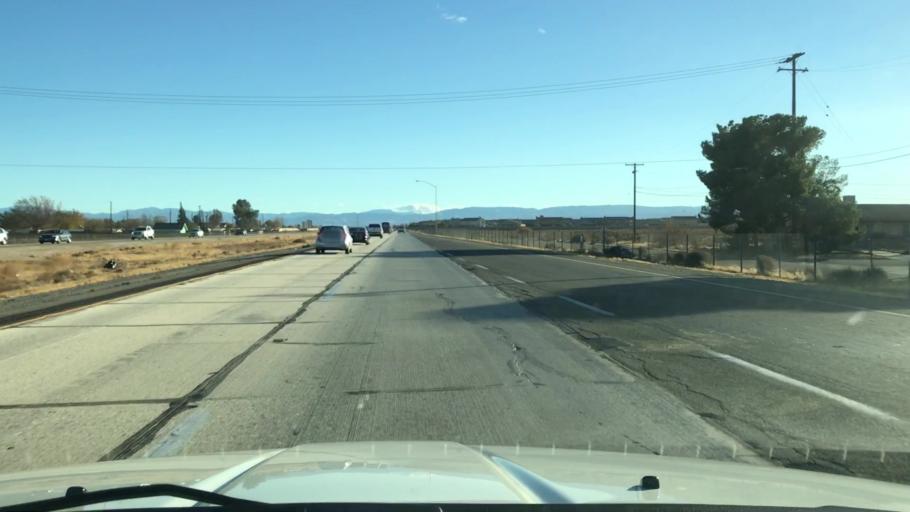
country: US
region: California
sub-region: Kern County
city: Rosamond
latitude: 34.8615
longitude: -118.1721
